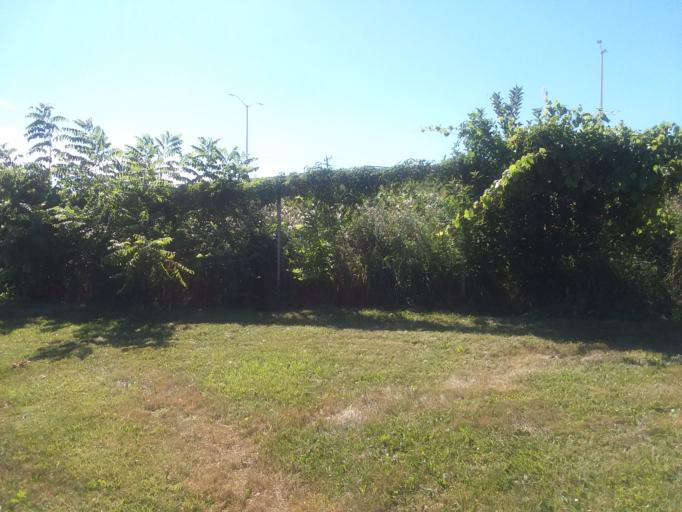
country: US
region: Wisconsin
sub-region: Milwaukee County
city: Saint Francis
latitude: 42.9446
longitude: -87.9203
